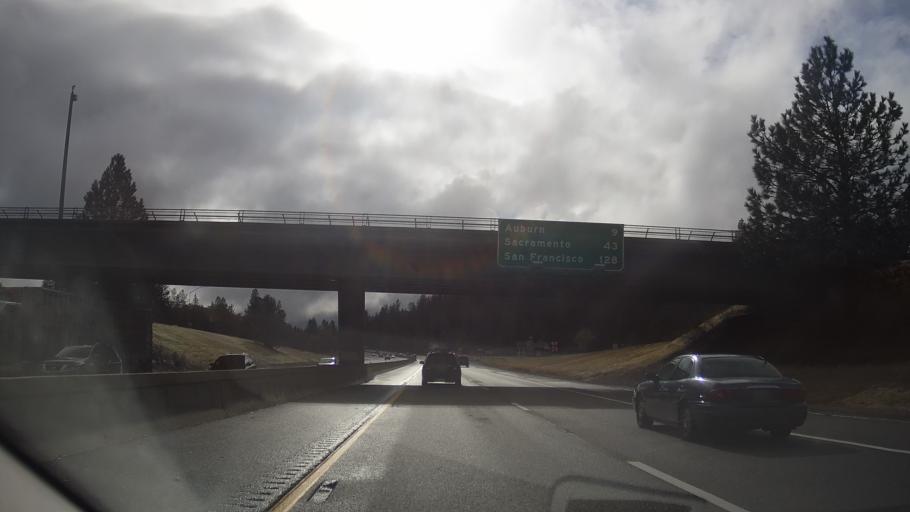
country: US
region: California
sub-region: Placer County
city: Meadow Vista
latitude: 39.0043
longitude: -120.9933
